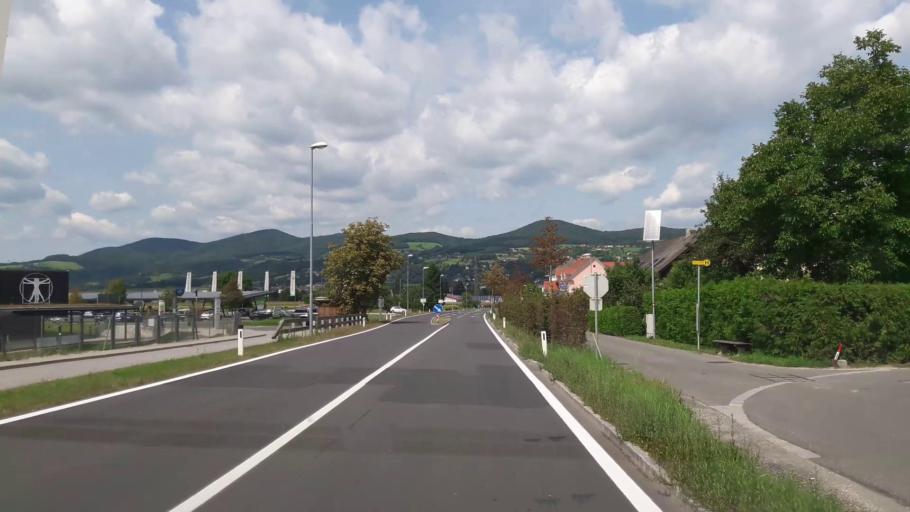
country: AT
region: Styria
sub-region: Politischer Bezirk Hartberg-Fuerstenfeld
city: Hartberg
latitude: 47.2597
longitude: 15.9725
